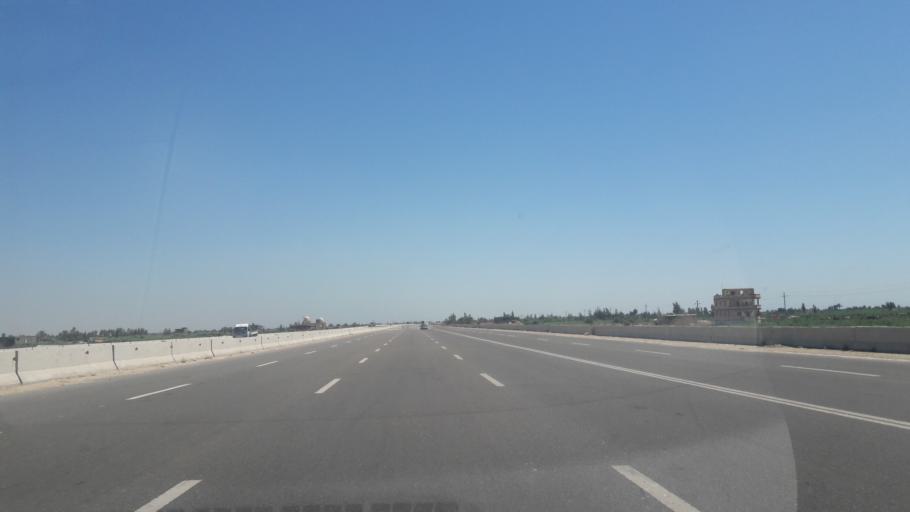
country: EG
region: Muhafazat Bur Sa`id
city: Port Said
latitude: 31.1701
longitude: 32.2355
